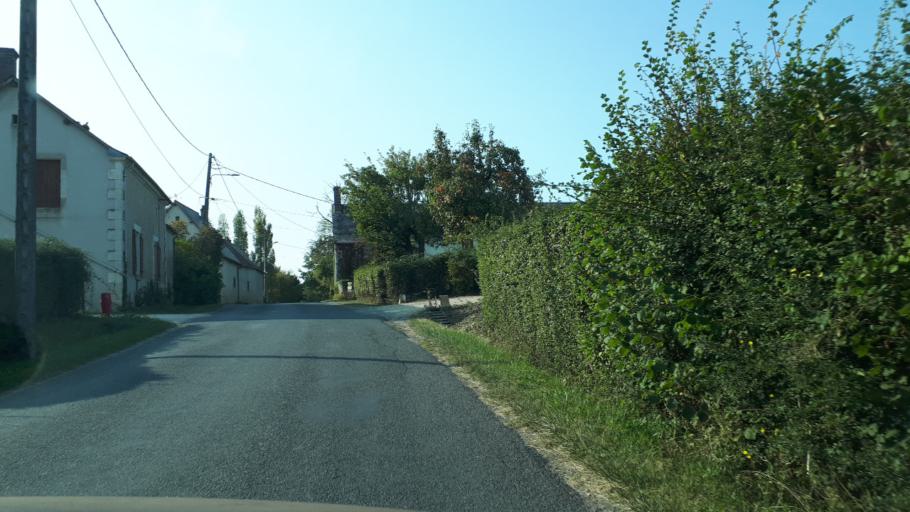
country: FR
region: Centre
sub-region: Departement du Cher
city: Menetou-Salon
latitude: 47.2219
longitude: 2.5321
